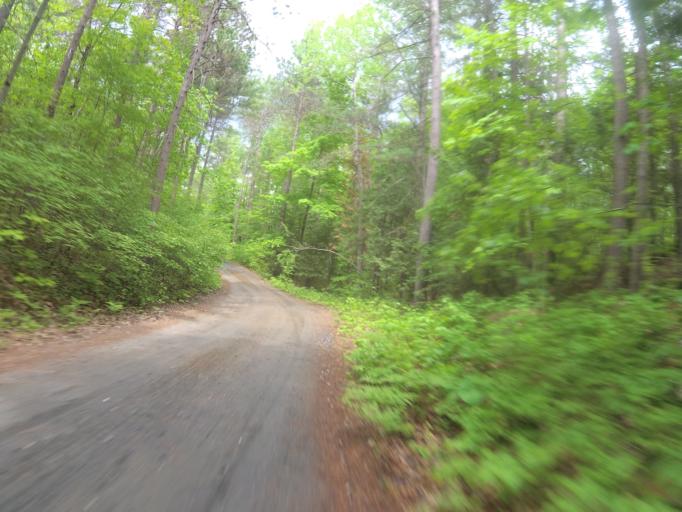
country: CA
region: Ontario
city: Renfrew
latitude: 45.0997
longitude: -76.8322
